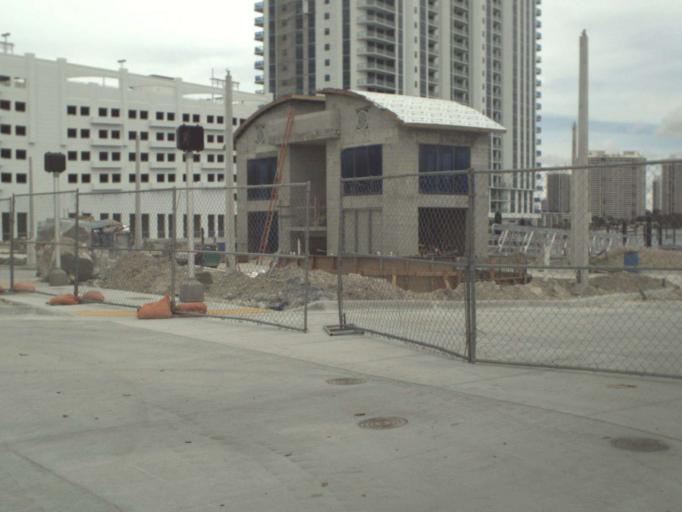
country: US
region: Florida
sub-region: Miami-Dade County
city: North Miami Beach
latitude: 25.9347
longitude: -80.1508
